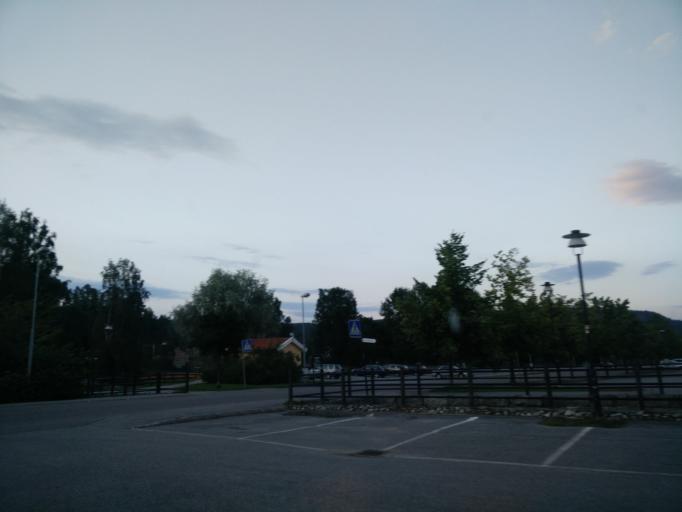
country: SE
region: Vaesternorrland
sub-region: Solleftea Kommun
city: Solleftea
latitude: 63.1674
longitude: 17.2710
